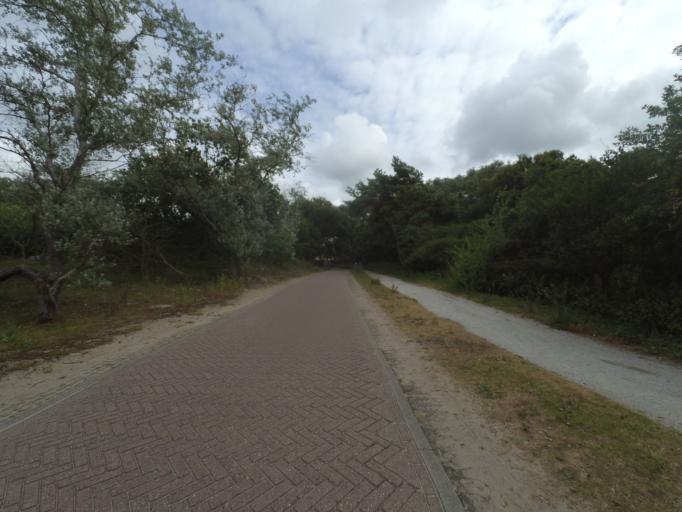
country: NL
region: South Holland
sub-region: Gemeente Den Haag
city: Scheveningen
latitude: 52.1300
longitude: 4.3319
